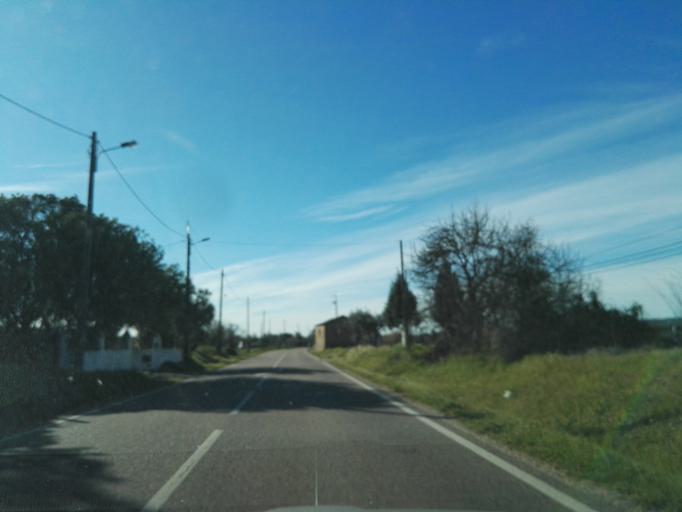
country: PT
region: Portalegre
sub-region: Gaviao
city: Gaviao
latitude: 39.4611
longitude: -8.0224
